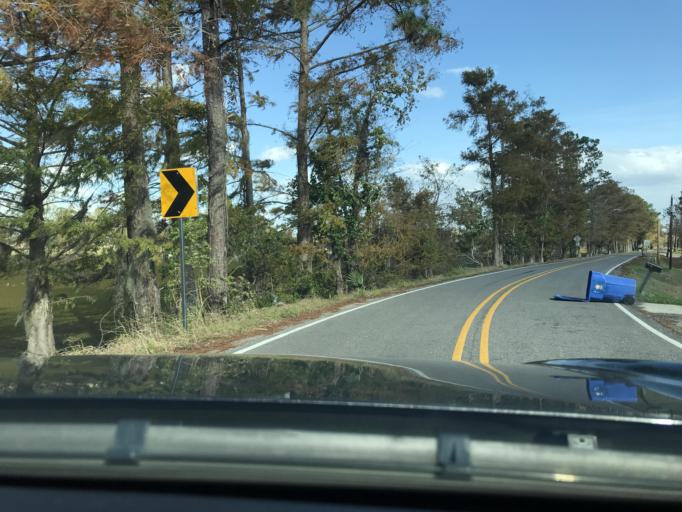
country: US
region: Louisiana
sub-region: Calcasieu Parish
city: Westlake
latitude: 30.3171
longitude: -93.2938
